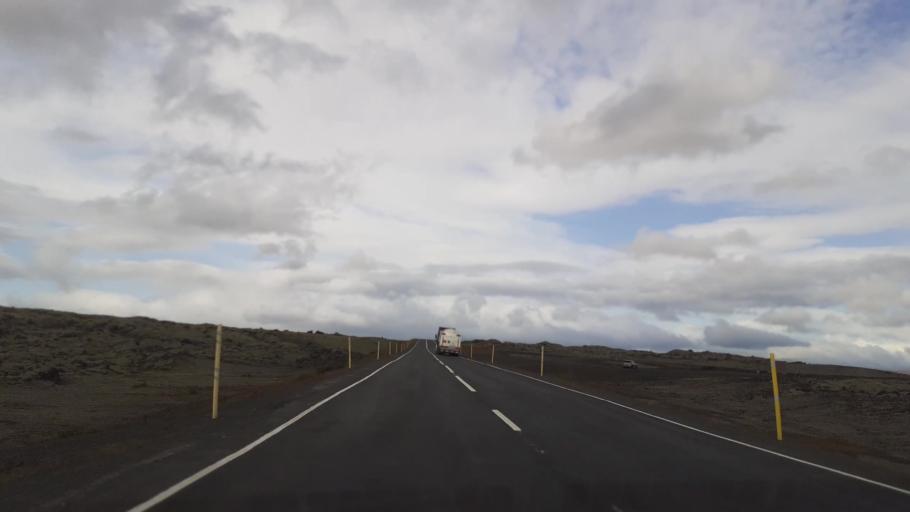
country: IS
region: South
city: THorlakshoefn
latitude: 64.0246
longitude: -21.4518
